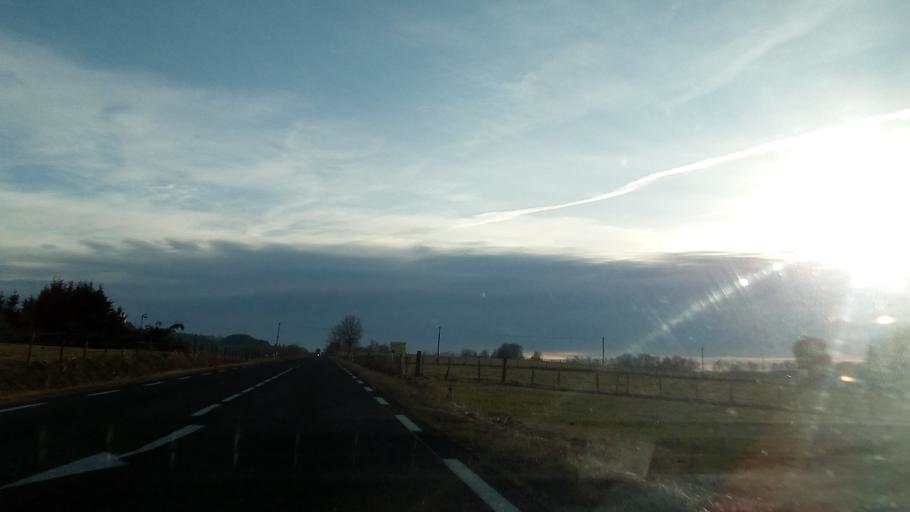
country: FR
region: Auvergne
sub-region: Departement du Puy-de-Dome
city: La Bourboule
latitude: 45.6379
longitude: 2.7232
